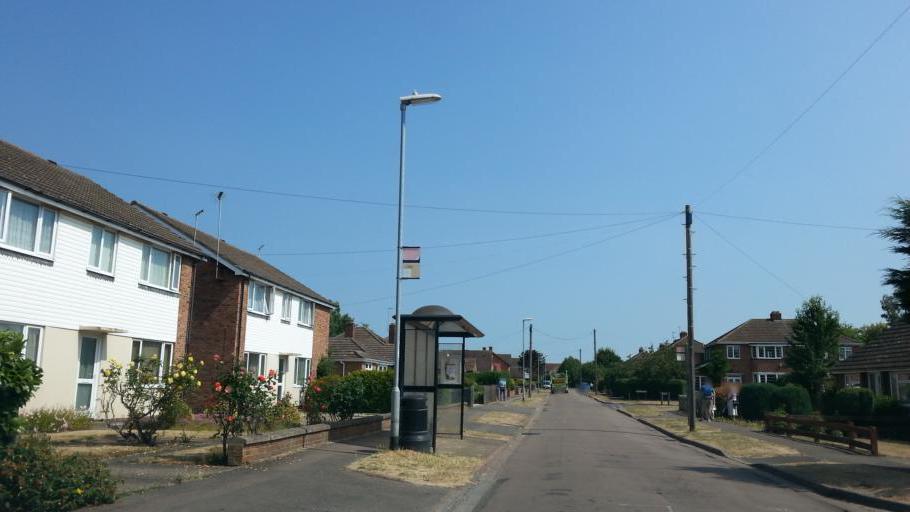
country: GB
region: England
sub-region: Cambridgeshire
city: Brampton
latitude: 52.3249
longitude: -0.2385
